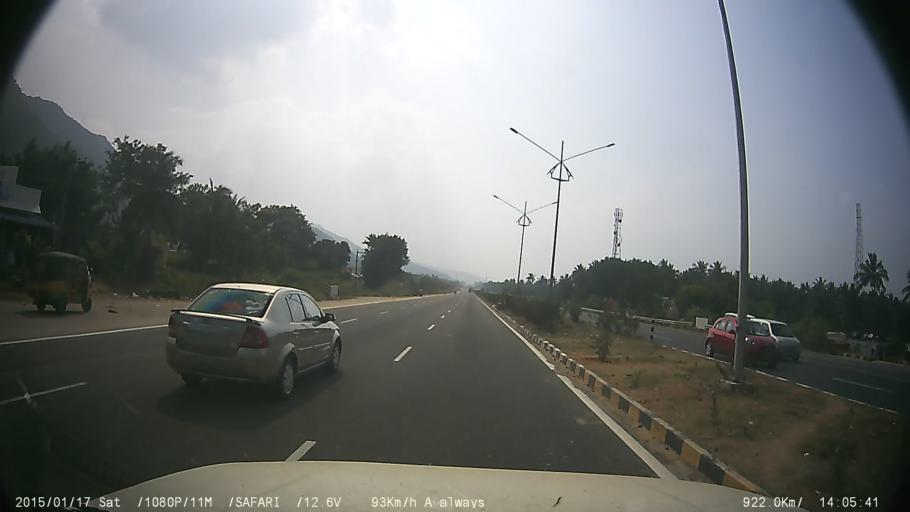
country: IN
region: Tamil Nadu
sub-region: Vellore
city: Ambur
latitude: 12.8460
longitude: 78.8037
